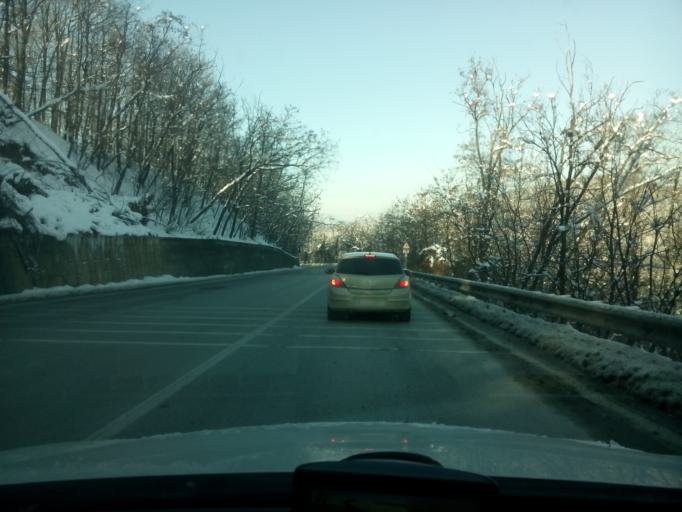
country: RO
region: Valcea
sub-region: Comuna Milcoiu
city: Milcoiu
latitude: 45.0551
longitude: 24.4549
